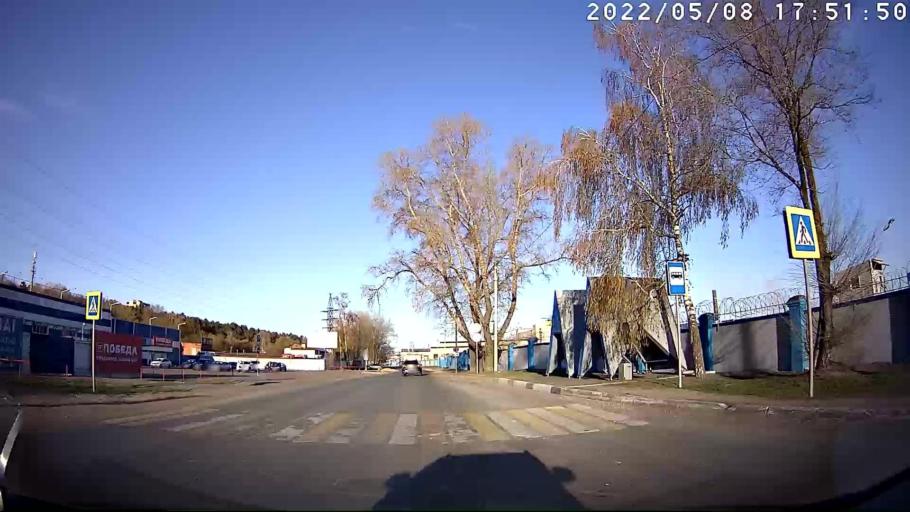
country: RU
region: Tatarstan
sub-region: Zelenodol'skiy Rayon
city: Zelenodolsk
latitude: 55.8406
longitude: 48.4982
